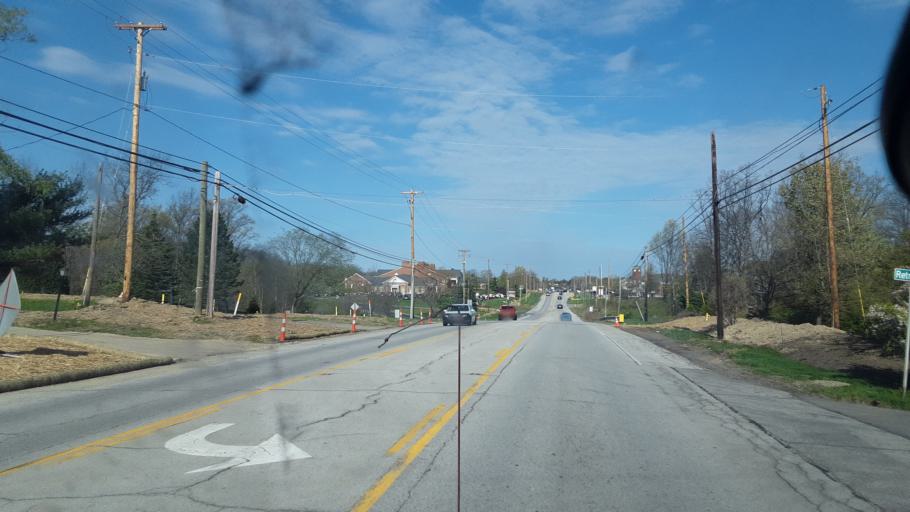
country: US
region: Ohio
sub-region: Medina County
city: Medina
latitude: 41.1375
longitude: -81.8256
